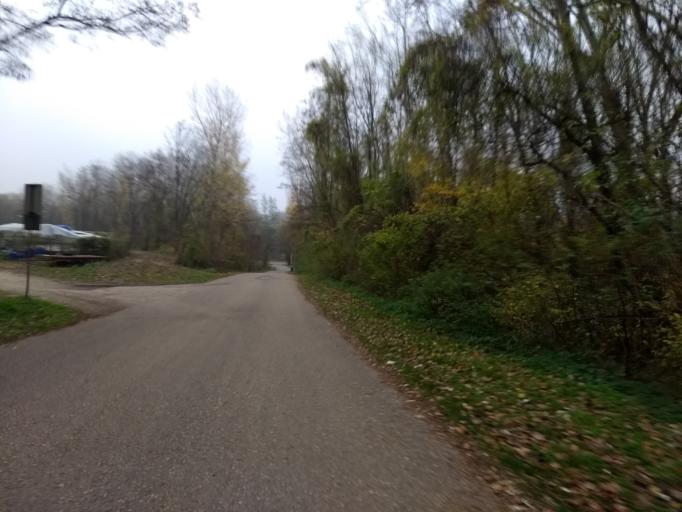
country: AT
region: Lower Austria
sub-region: Politischer Bezirk Tulln
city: Wordern
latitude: 48.3467
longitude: 16.2127
